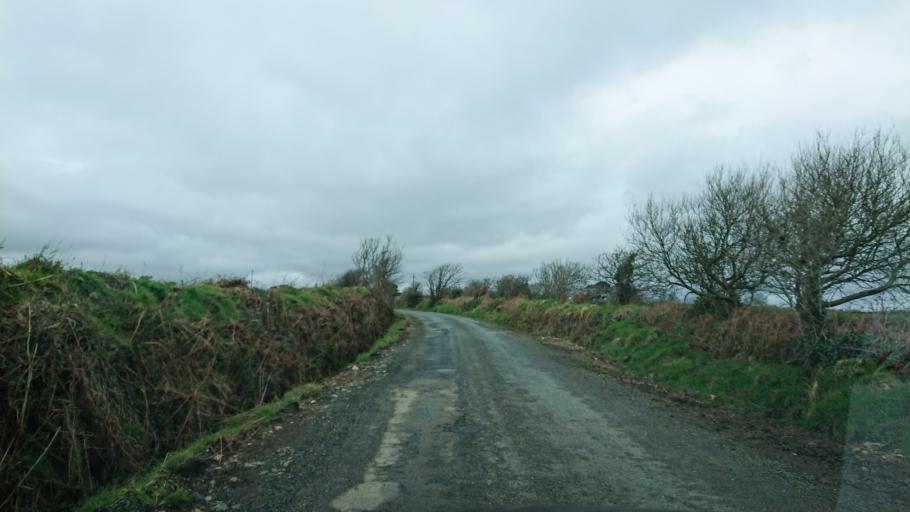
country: IE
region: Munster
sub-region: Waterford
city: Dunmore East
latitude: 52.1705
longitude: -7.0430
